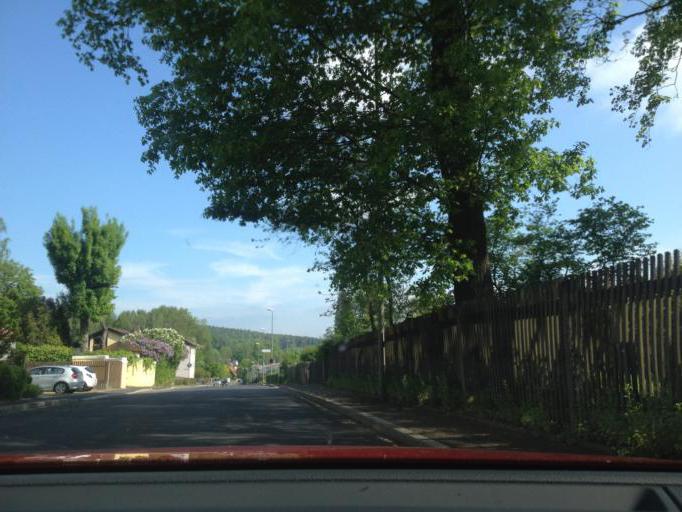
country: DE
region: Bavaria
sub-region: Upper Franconia
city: Marktredwitz
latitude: 50.0084
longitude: 12.0846
